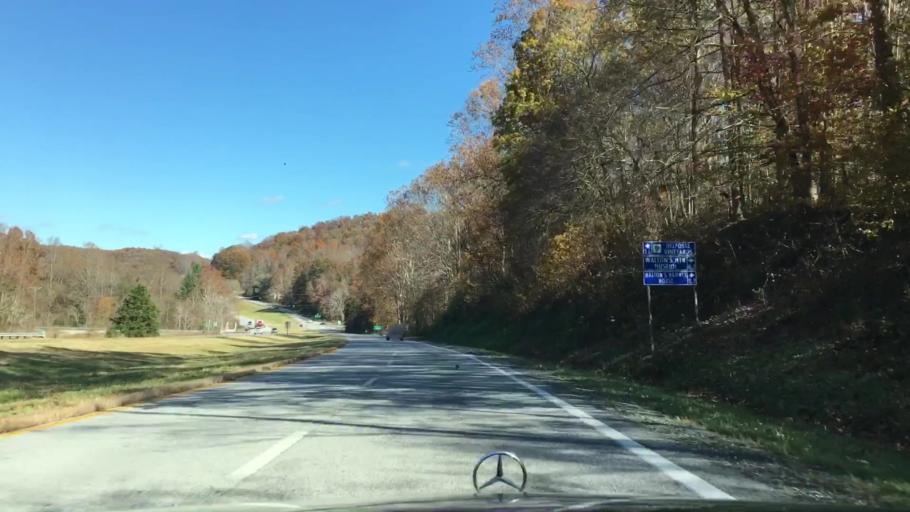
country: US
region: Virginia
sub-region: Nelson County
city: Nellysford
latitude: 37.8477
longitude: -78.7594
